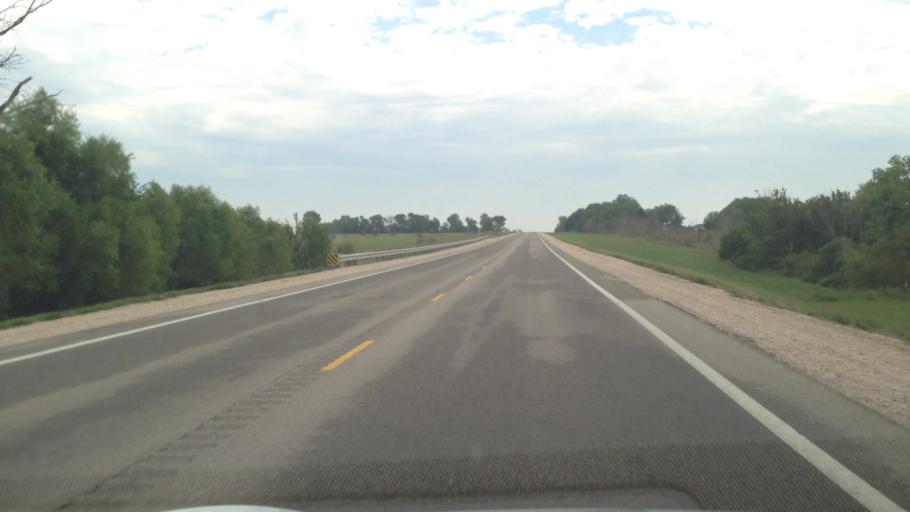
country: US
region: Kansas
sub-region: Allen County
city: Iola
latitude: 37.9094
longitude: -95.1141
